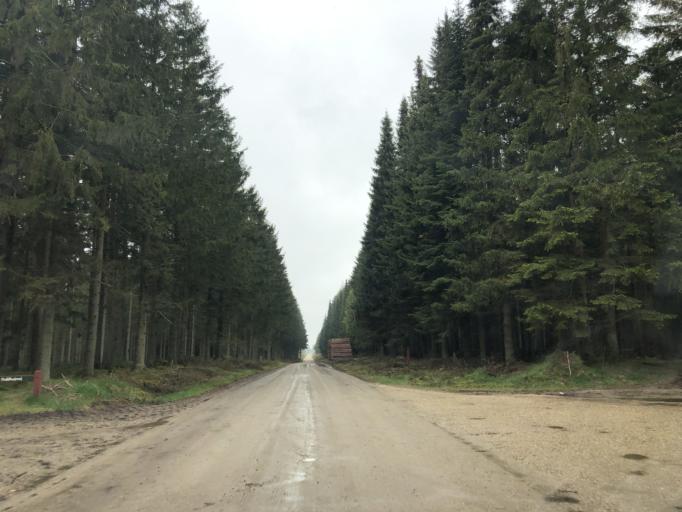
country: DK
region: Central Jutland
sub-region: Lemvig Kommune
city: Lemvig
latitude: 56.4890
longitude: 8.3530
